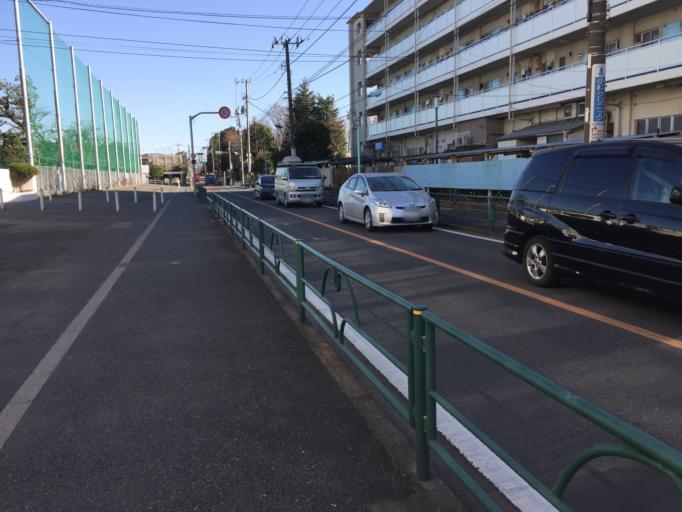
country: JP
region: Tokyo
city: Chofugaoka
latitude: 35.6254
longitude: 139.5940
